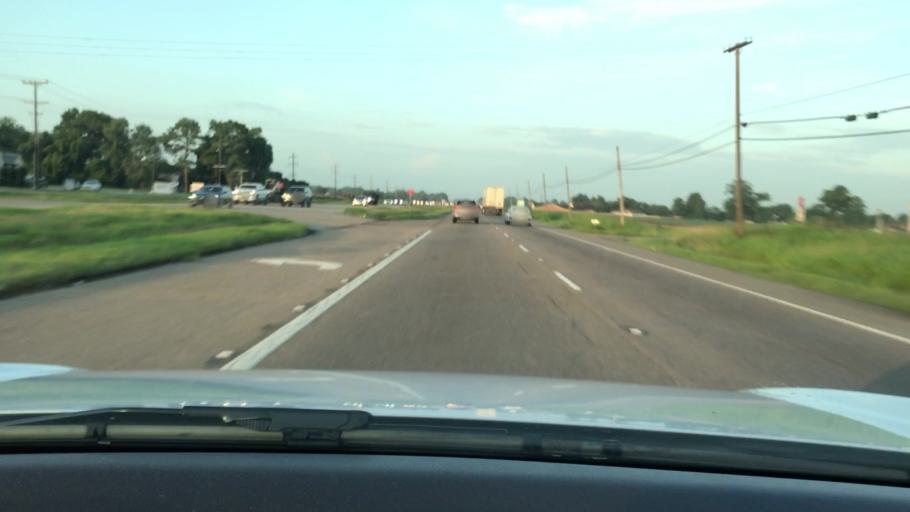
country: US
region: Louisiana
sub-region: West Baton Rouge Parish
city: Brusly
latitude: 30.4068
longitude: -91.2302
